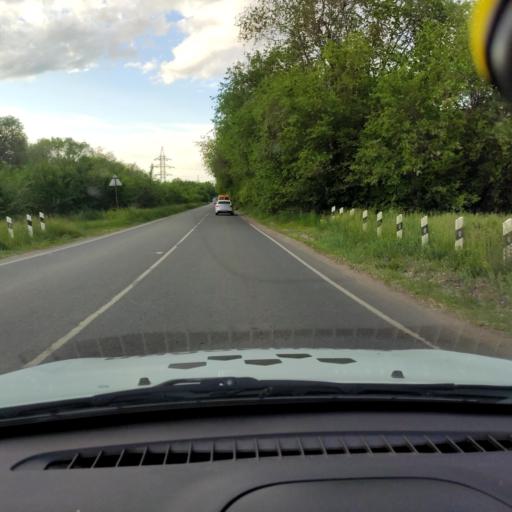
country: RU
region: Samara
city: Tol'yatti
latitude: 53.5789
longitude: 49.2557
